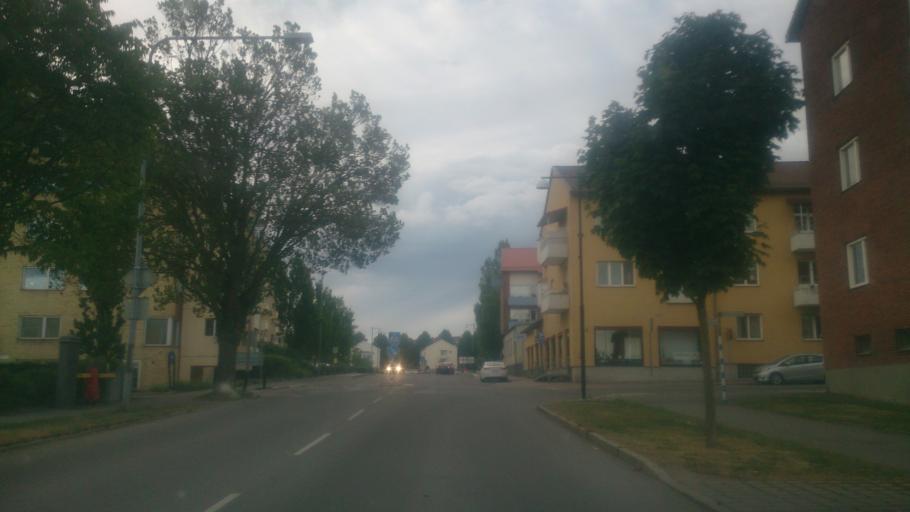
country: SE
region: OEstergoetland
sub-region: Motala Kommun
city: Motala
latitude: 58.5362
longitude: 15.0328
